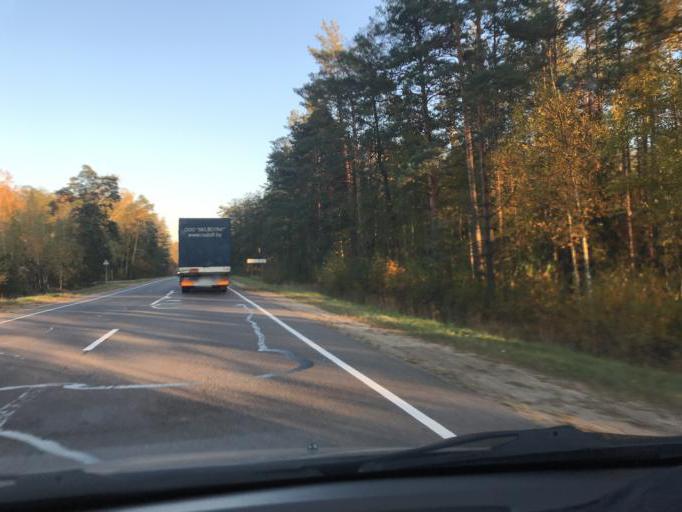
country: BY
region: Minsk
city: Staryya Darohi
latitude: 53.0362
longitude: 28.2188
